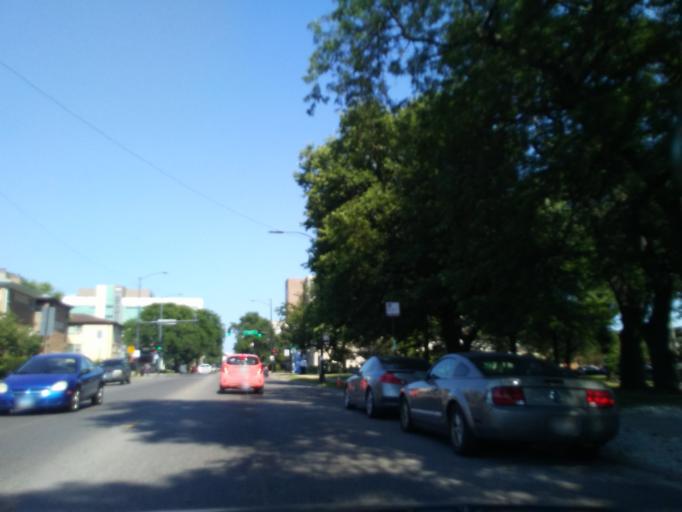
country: US
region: Illinois
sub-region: Cook County
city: Lincolnwood
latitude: 41.9758
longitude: -87.7023
